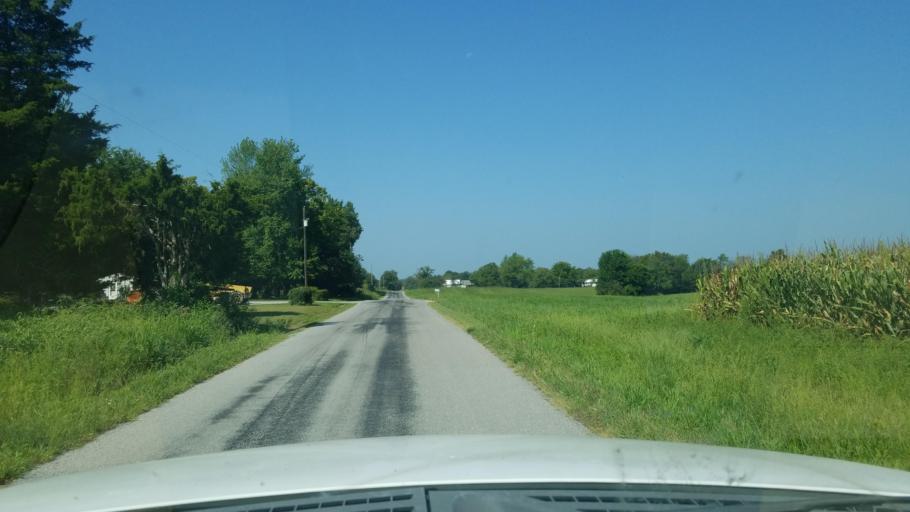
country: US
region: Illinois
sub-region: Saline County
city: Harrisburg
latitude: 37.8922
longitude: -88.6556
